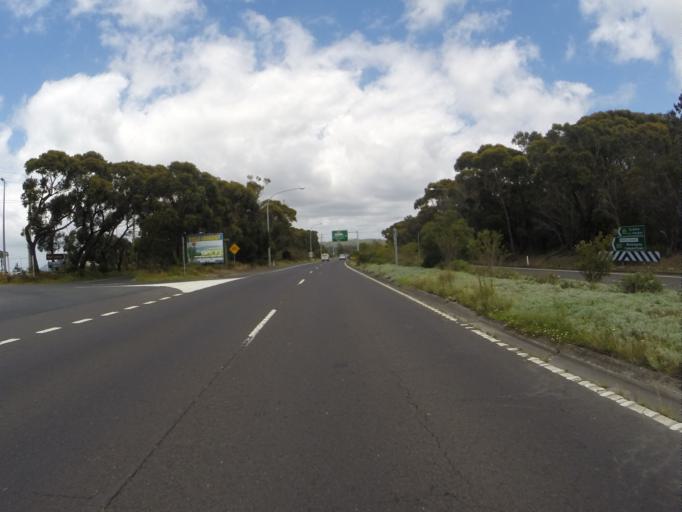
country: AU
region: New South Wales
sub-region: Wollongong
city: Bulli
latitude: -34.3023
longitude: 150.9099
